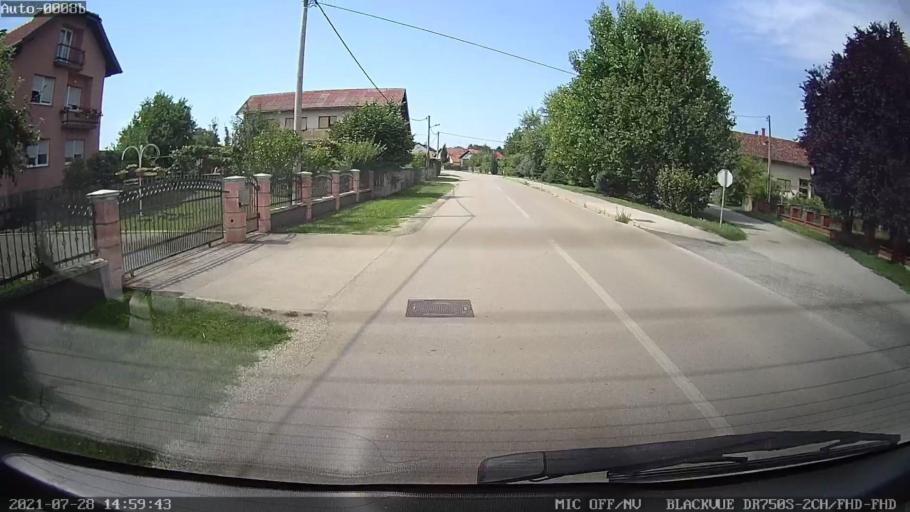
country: HR
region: Medimurska
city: Kursanec
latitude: 46.2838
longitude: 16.3875
